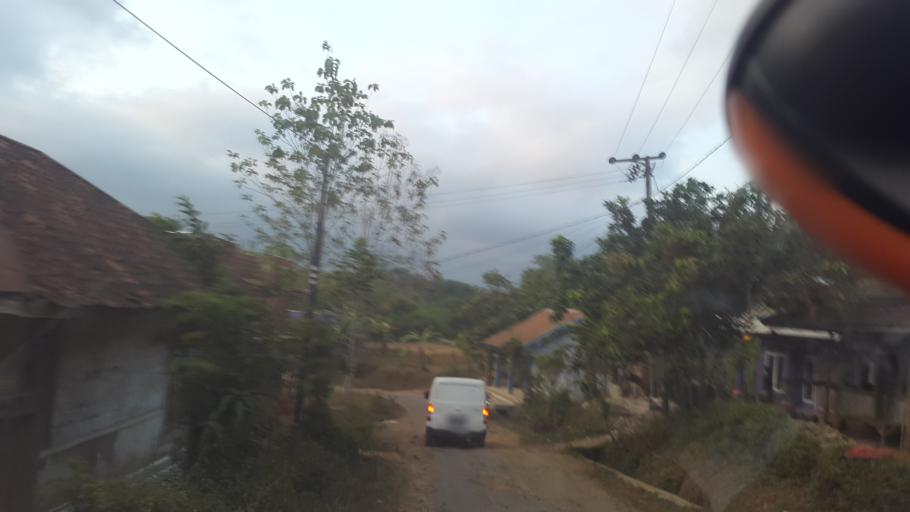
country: ID
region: West Java
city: Datarnangka
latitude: -7.2061
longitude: 106.8486
